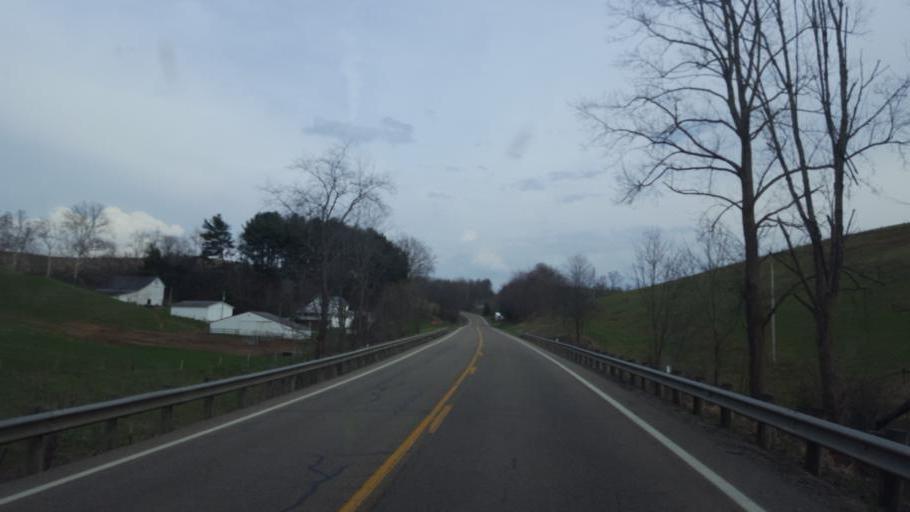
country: US
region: Ohio
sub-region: Coshocton County
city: Coshocton
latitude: 40.1635
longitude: -81.8145
